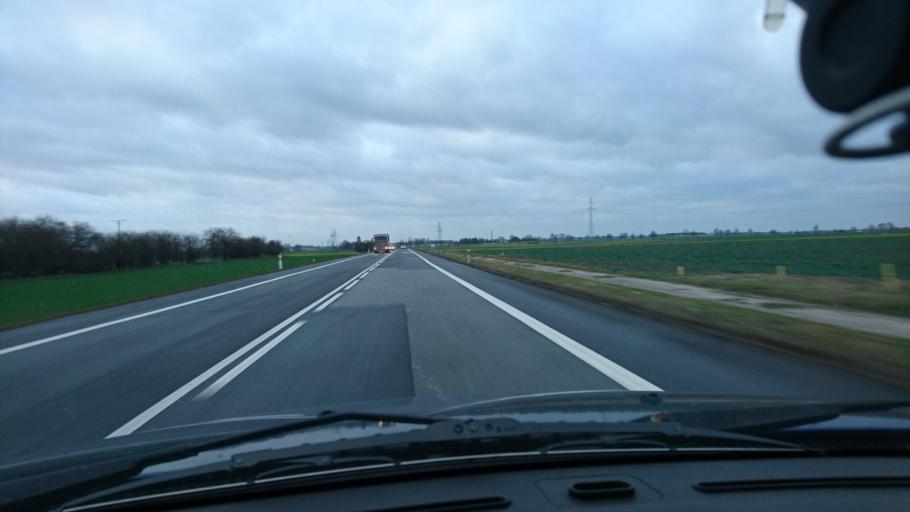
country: PL
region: Opole Voivodeship
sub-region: Powiat kluczborski
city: Kluczbork
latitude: 50.9895
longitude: 18.2305
